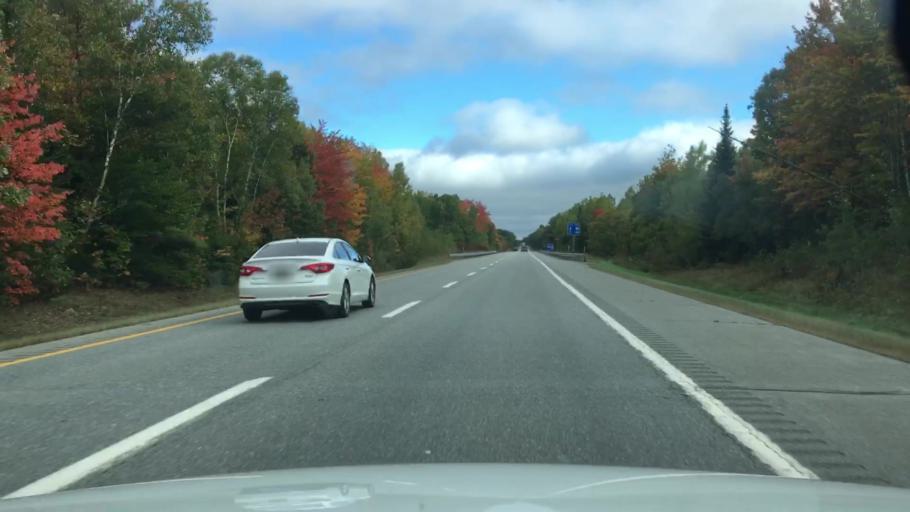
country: US
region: Maine
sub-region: Penobscot County
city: Carmel
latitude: 44.7673
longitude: -68.9962
